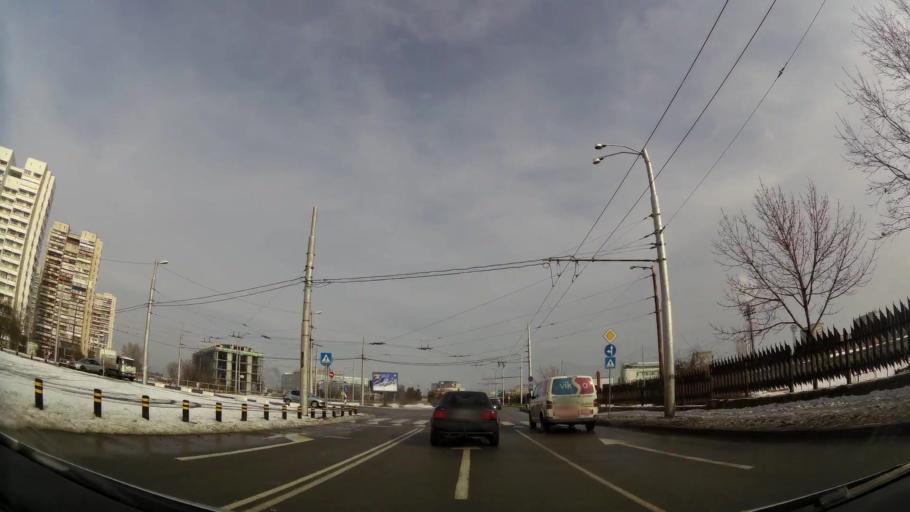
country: BG
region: Sofia-Capital
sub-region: Stolichna Obshtina
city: Sofia
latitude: 42.7071
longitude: 23.3634
